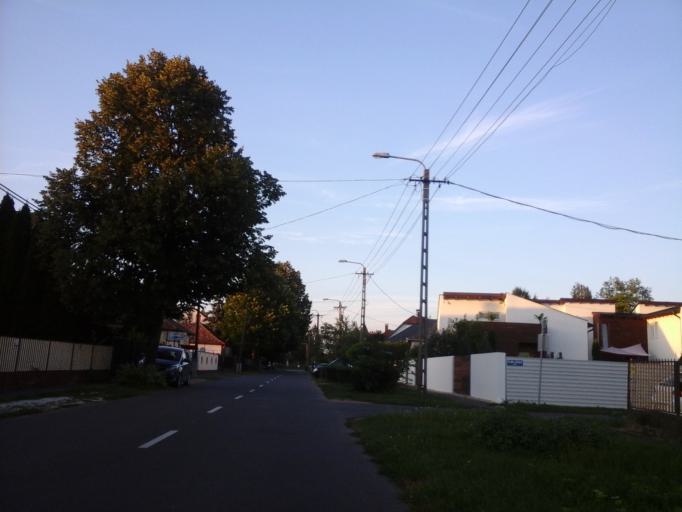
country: HU
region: Hajdu-Bihar
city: Hajduszoboszlo
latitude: 47.4579
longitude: 21.4103
